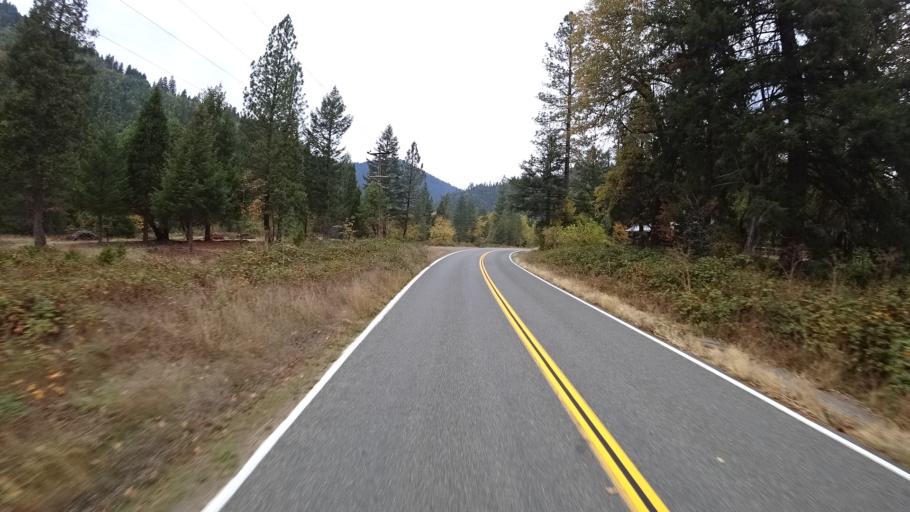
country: US
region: California
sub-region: Siskiyou County
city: Happy Camp
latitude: 41.8778
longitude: -123.4192
